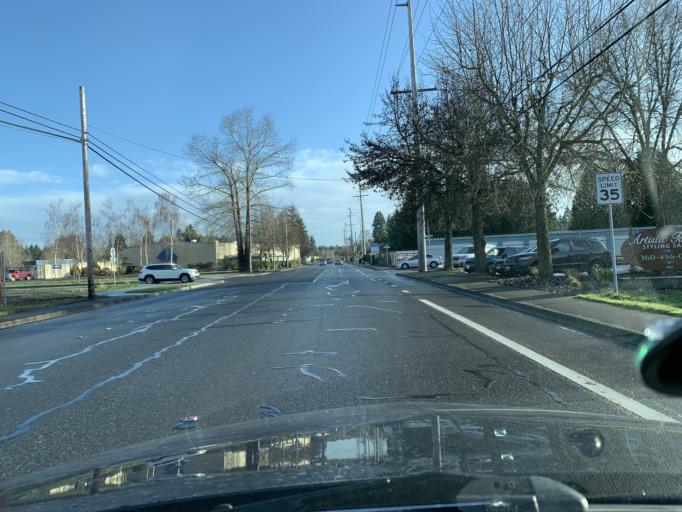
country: US
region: Washington
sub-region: Thurston County
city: Lacey
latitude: 47.0358
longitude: -122.8111
